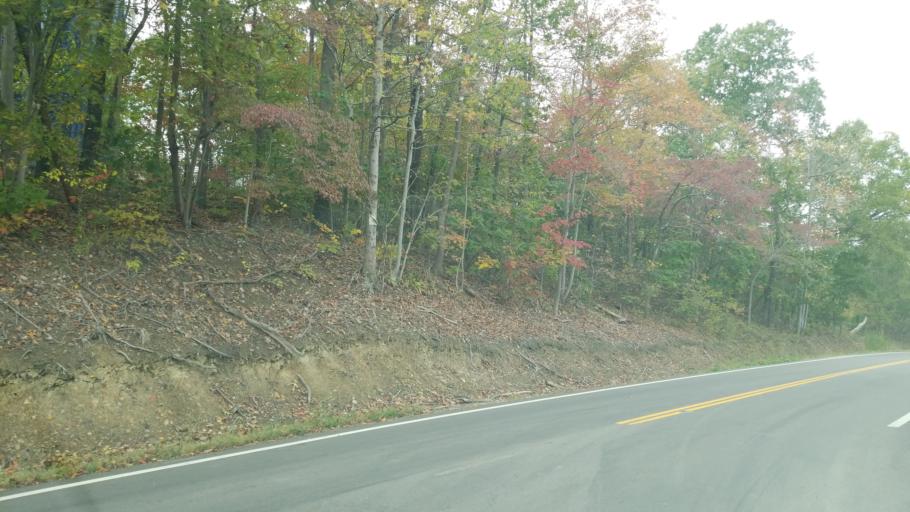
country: US
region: Ohio
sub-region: Jackson County
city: Wellston
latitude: 39.1545
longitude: -82.5985
